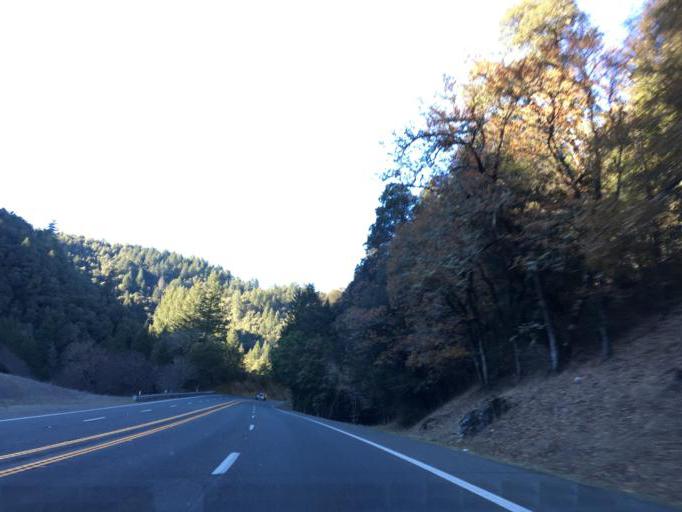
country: US
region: California
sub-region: Mendocino County
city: Laytonville
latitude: 39.5793
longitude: -123.4417
